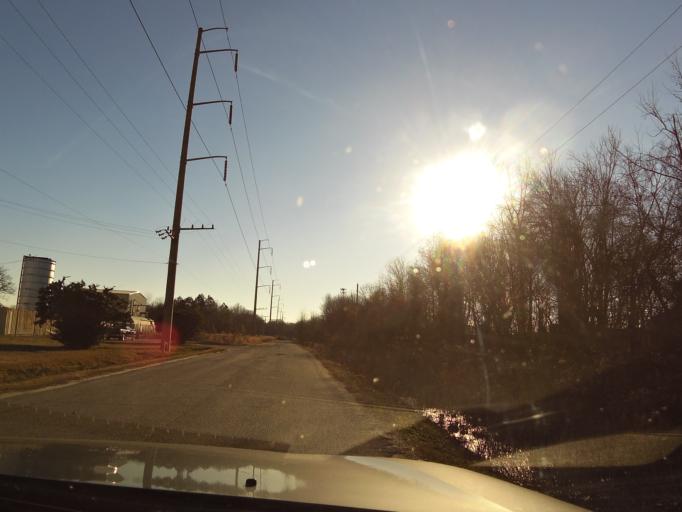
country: US
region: Virginia
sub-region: City of Hopewell
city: Hopewell
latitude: 37.2916
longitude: -77.2779
